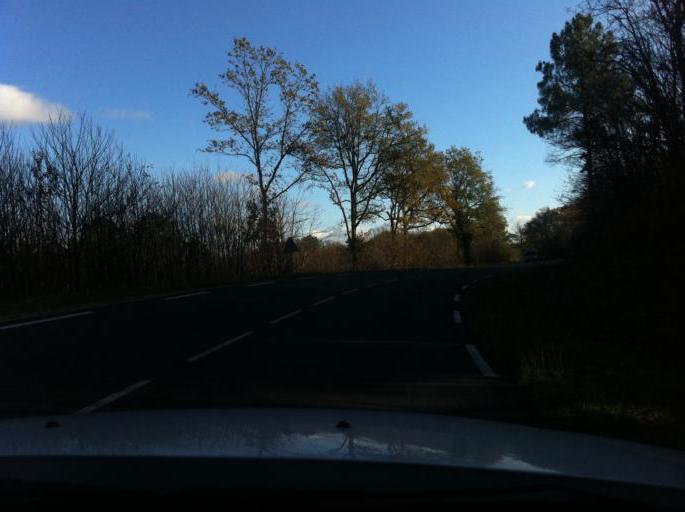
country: FR
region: Aquitaine
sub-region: Departement de la Dordogne
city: Rouffignac-Saint-Cernin-de-Reilhac
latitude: 45.0405
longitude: 0.8683
